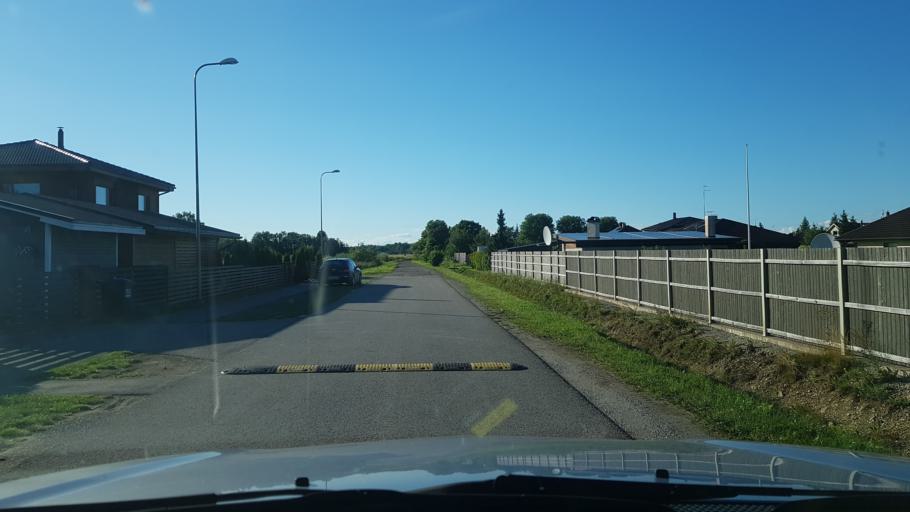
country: EE
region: Harju
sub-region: Rae vald
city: Jueri
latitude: 59.3902
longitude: 24.8538
